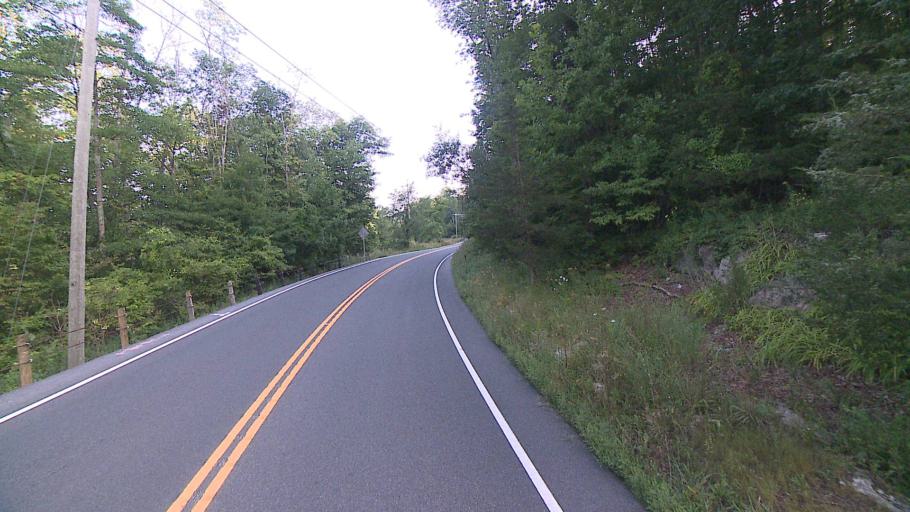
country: US
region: Connecticut
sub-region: Litchfield County
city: Kent
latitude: 41.6533
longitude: -73.4895
